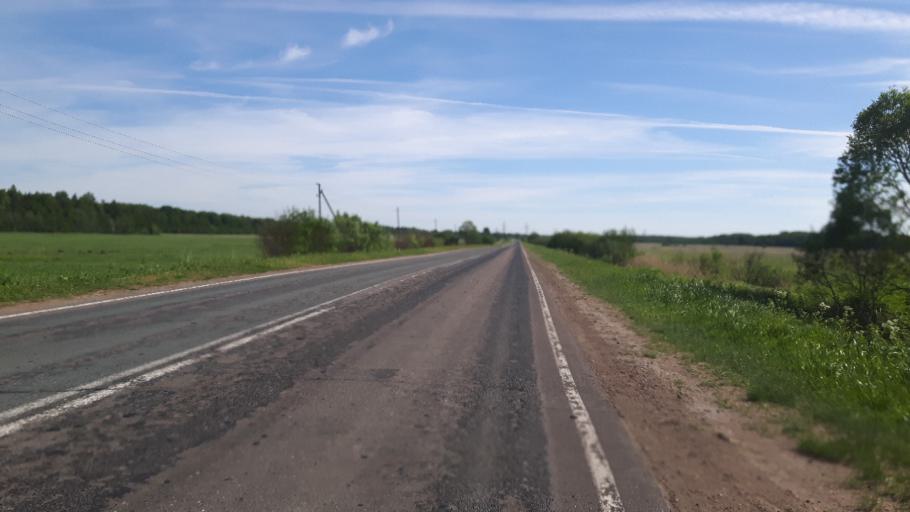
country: RU
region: Leningrad
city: Ivangorod
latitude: 59.4104
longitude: 28.3844
